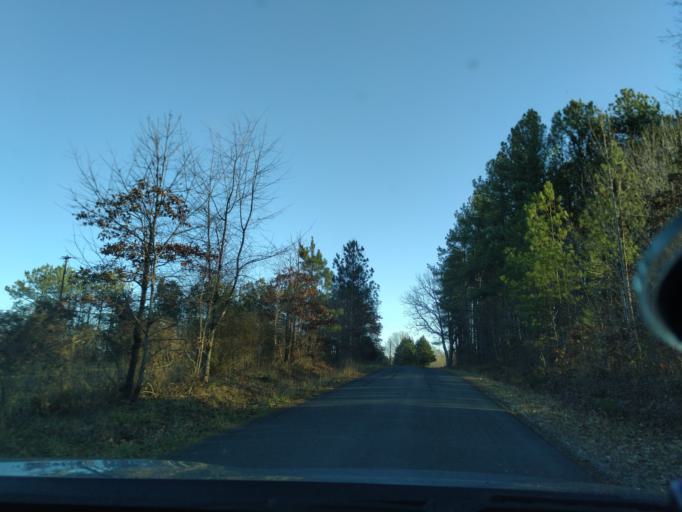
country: US
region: Virginia
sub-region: Buckingham County
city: Buckingham
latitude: 37.3691
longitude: -78.6171
